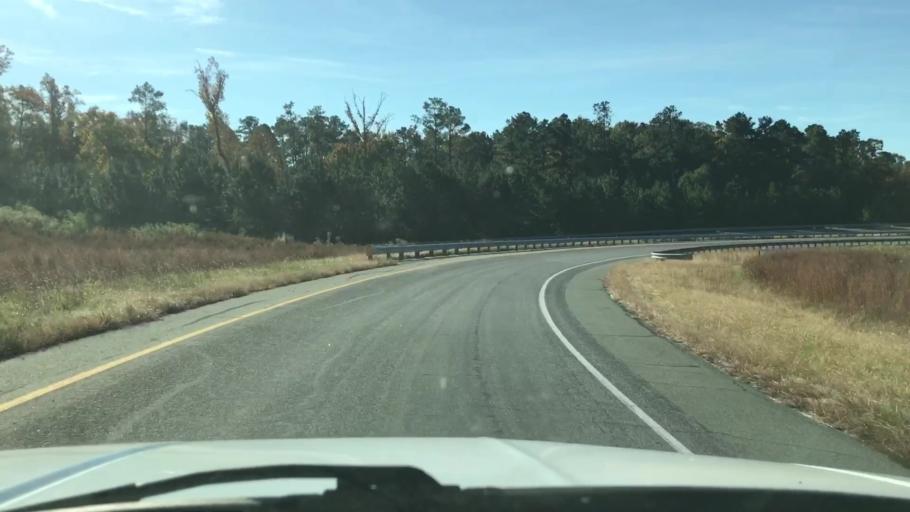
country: US
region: Virginia
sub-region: Henrico County
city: Short Pump
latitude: 37.5990
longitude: -77.6643
